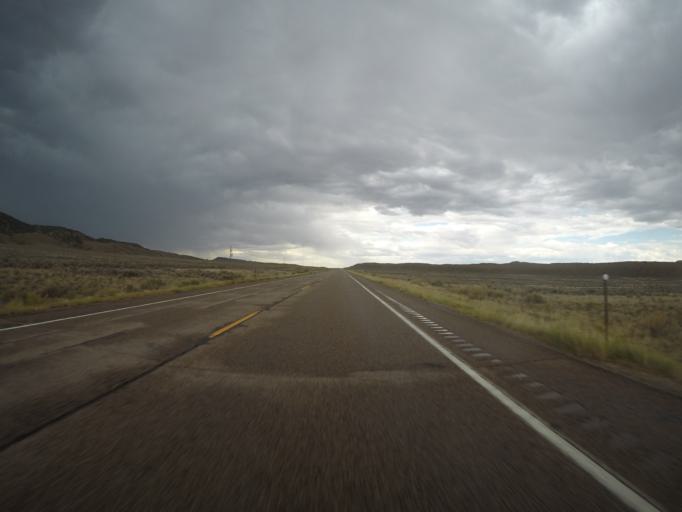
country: US
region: Colorado
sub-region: Rio Blanco County
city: Rangely
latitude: 40.2514
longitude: -108.8520
